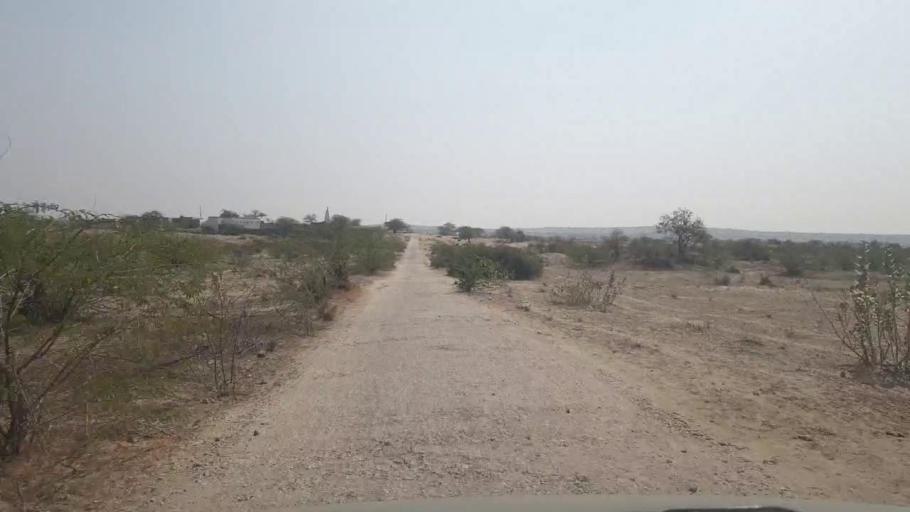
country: PK
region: Sindh
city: Chor
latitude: 25.4593
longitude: 69.7860
